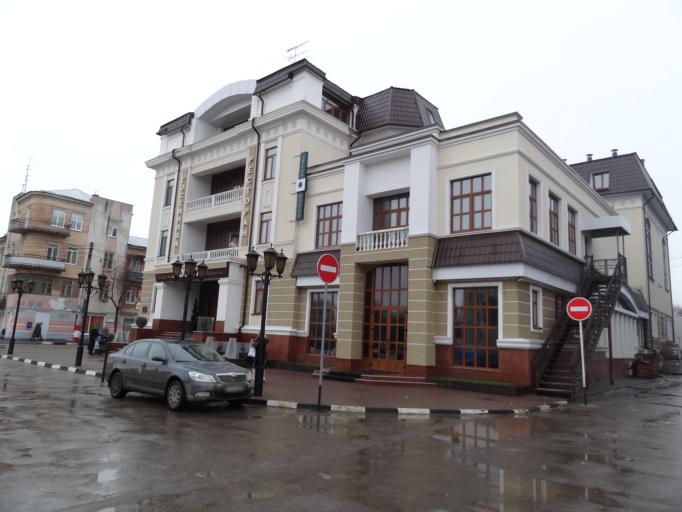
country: RU
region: Saratov
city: Engel's
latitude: 51.5027
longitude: 46.1194
